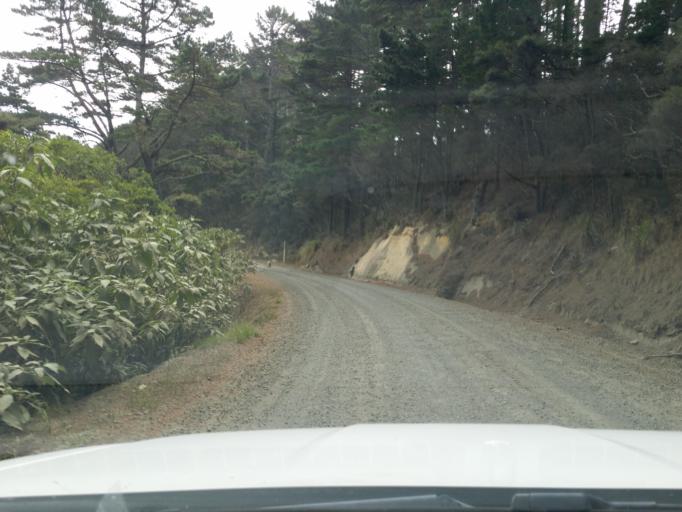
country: NZ
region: Auckland
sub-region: Auckland
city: Wellsford
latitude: -36.3121
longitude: 174.1288
